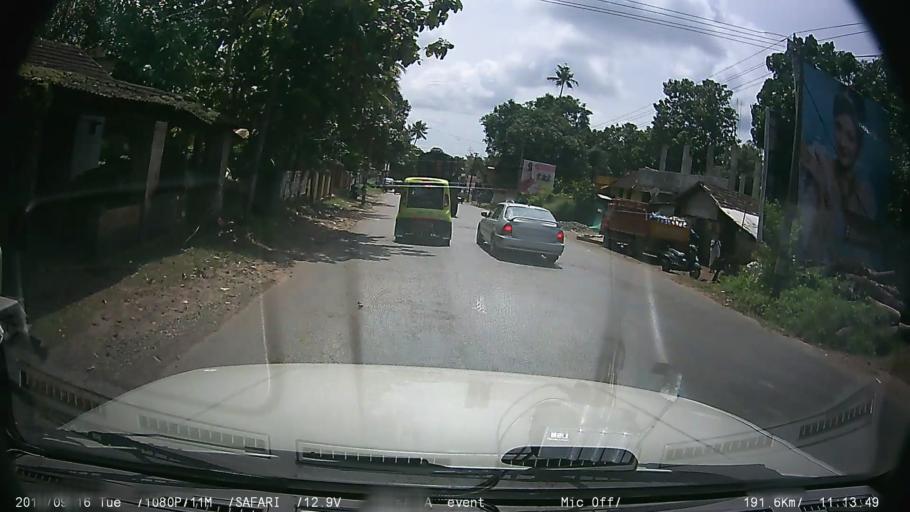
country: IN
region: Kerala
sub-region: Kottayam
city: Kottayam
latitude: 9.5162
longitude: 76.5254
